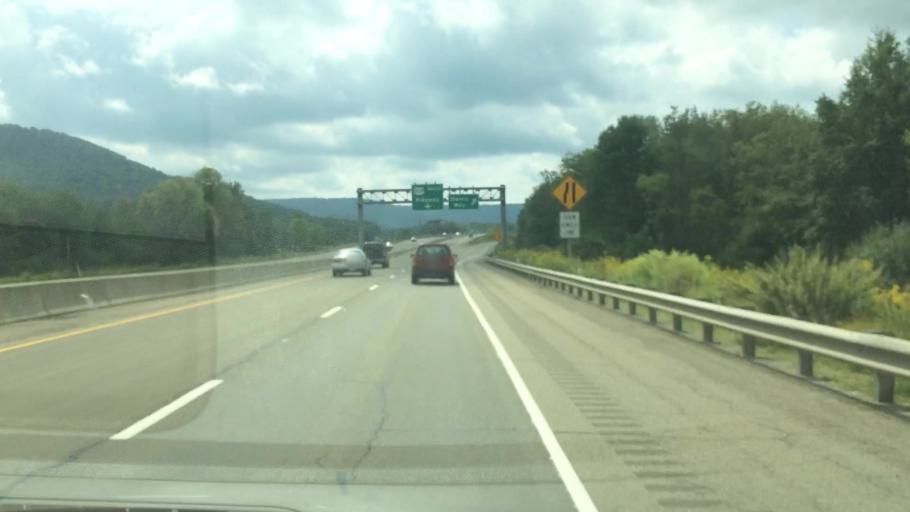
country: US
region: Pennsylvania
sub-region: McKean County
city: Bradford
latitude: 41.9346
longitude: -78.6493
